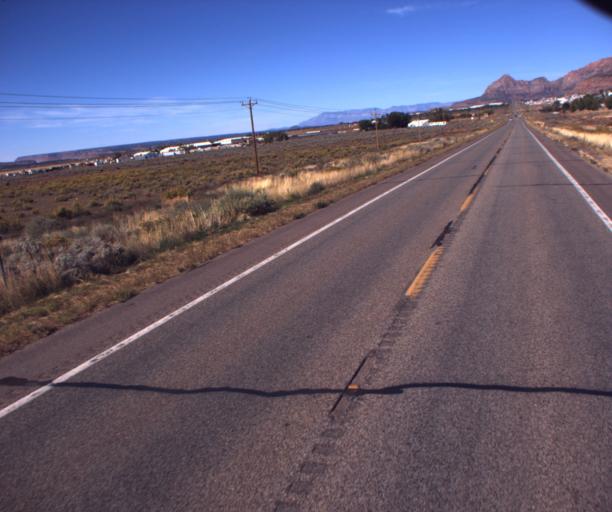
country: US
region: Arizona
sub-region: Mohave County
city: Colorado City
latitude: 36.9788
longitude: -112.9816
